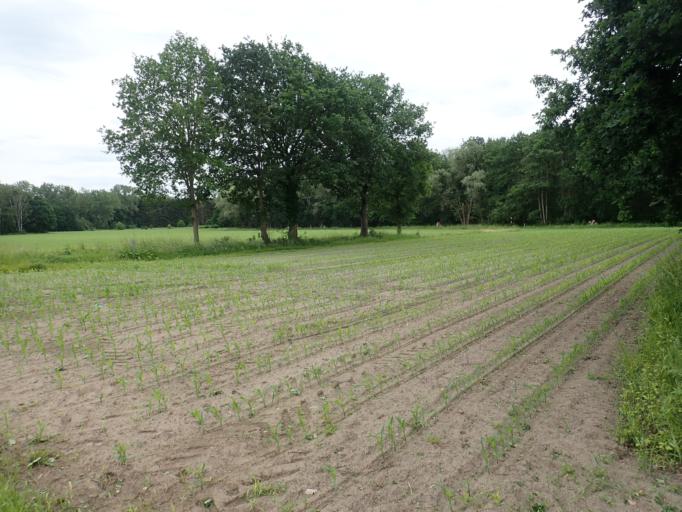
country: BE
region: Flanders
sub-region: Provincie Vlaams-Brabant
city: Haacht
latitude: 50.9713
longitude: 4.6450
